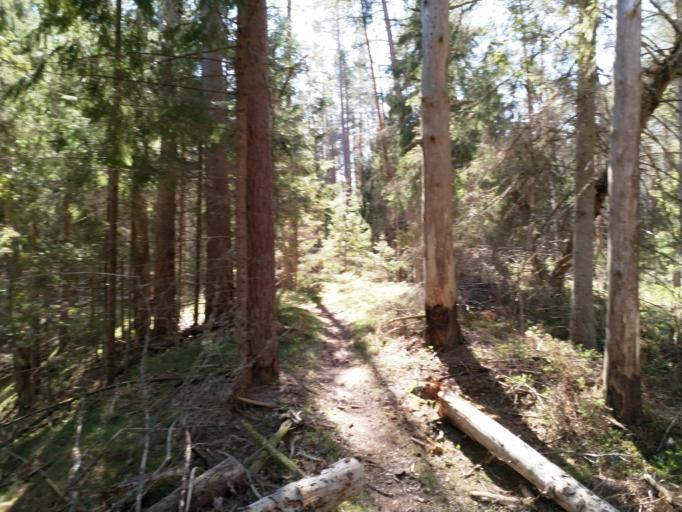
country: LV
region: Pavilostas
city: Pavilosta
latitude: 56.9615
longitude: 21.3559
